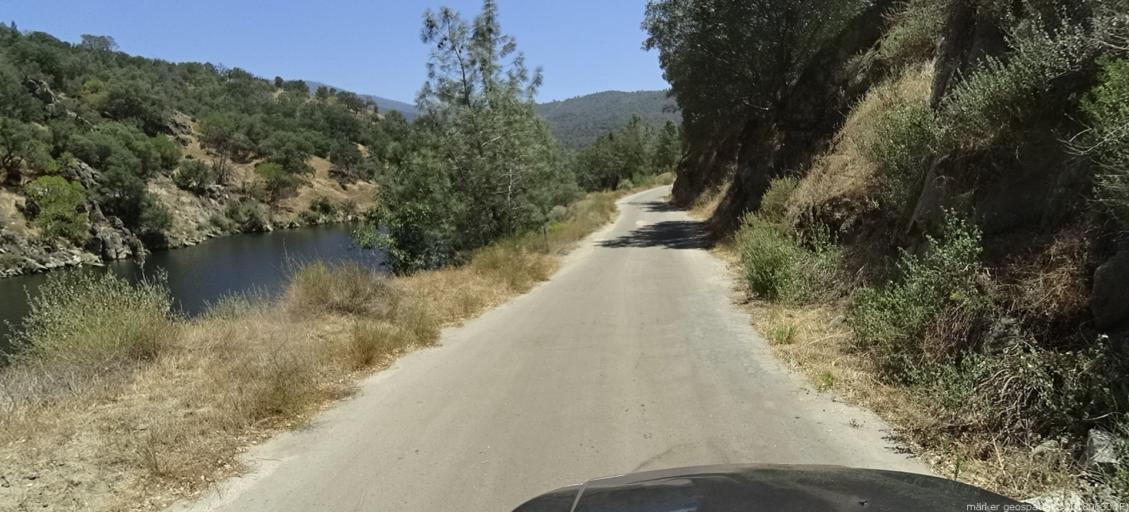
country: US
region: California
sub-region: Fresno County
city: Auberry
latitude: 37.1573
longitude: -119.4049
